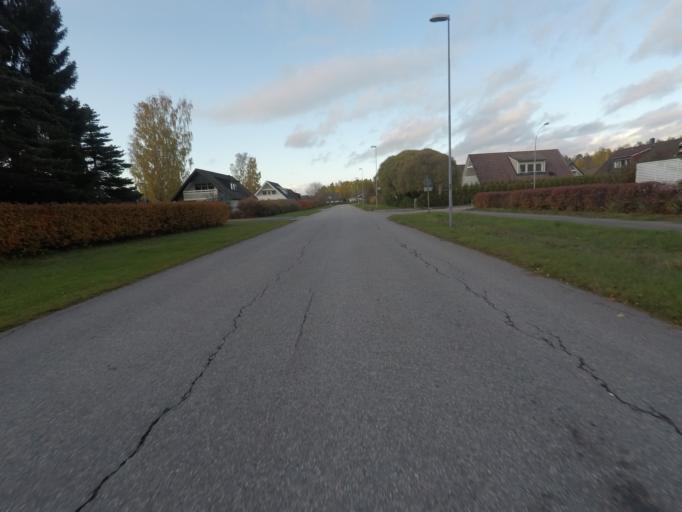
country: SE
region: OErebro
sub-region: Karlskoga Kommun
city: Karlskoga
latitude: 59.3078
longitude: 14.4759
